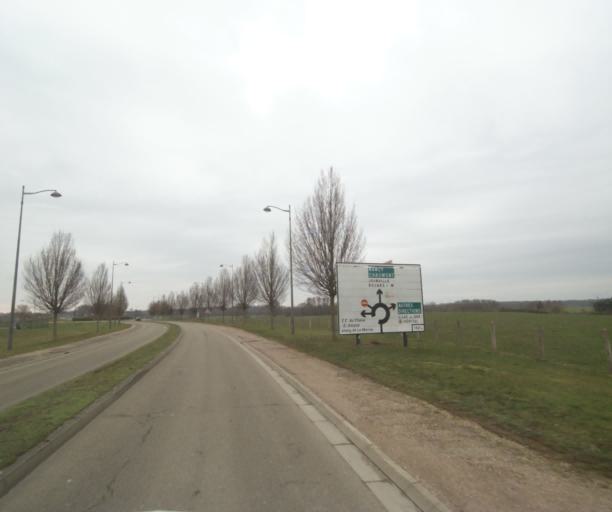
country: FR
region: Champagne-Ardenne
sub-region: Departement de la Haute-Marne
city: Saint-Dizier
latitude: 48.6249
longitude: 4.9622
